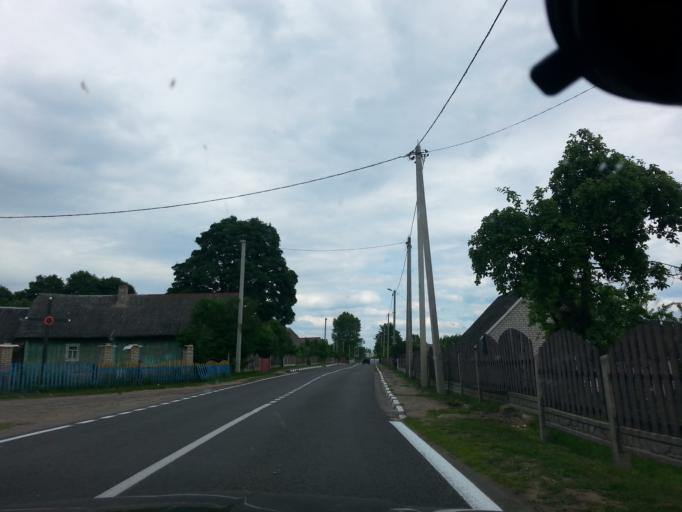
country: BY
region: Minsk
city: Narach
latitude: 54.8959
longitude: 26.7620
